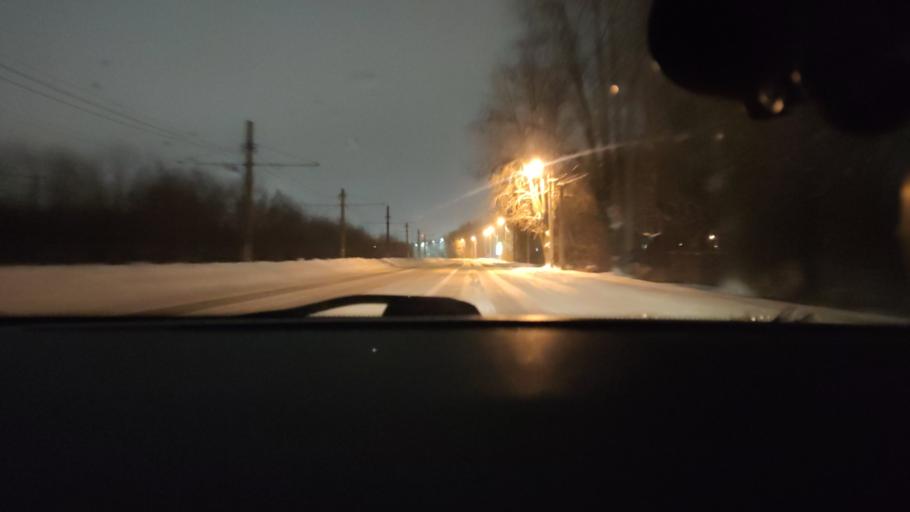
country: RU
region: Perm
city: Kondratovo
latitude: 57.9402
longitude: 56.1241
